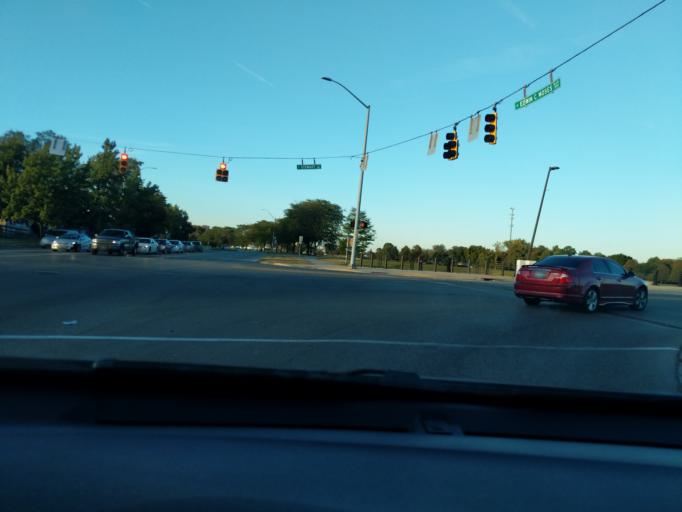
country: US
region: Ohio
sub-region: Montgomery County
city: Dayton
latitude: 39.7398
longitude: -84.1949
